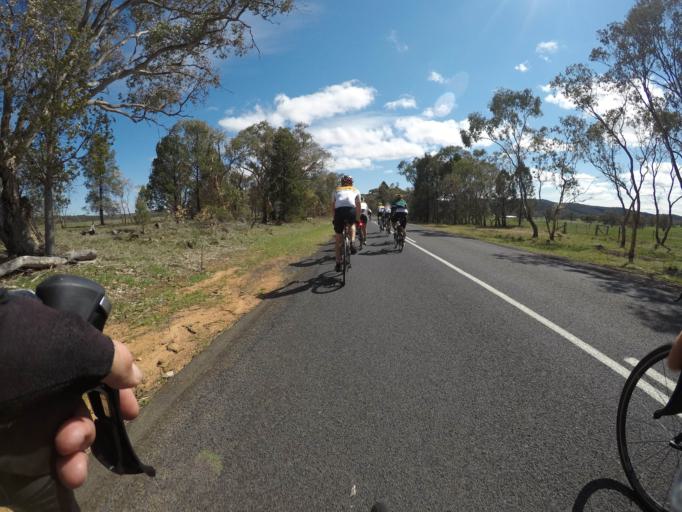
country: AU
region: New South Wales
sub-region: Parkes
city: Peak Hill
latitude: -32.6723
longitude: 148.5611
